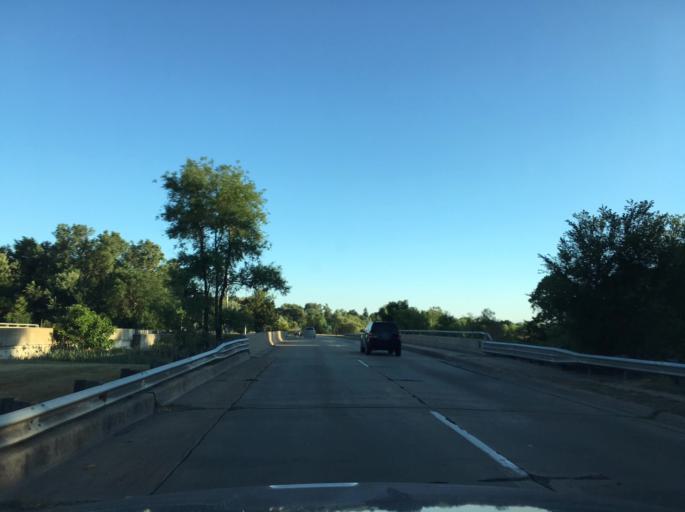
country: US
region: Michigan
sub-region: Macomb County
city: Sterling Heights
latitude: 42.5858
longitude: -82.9927
